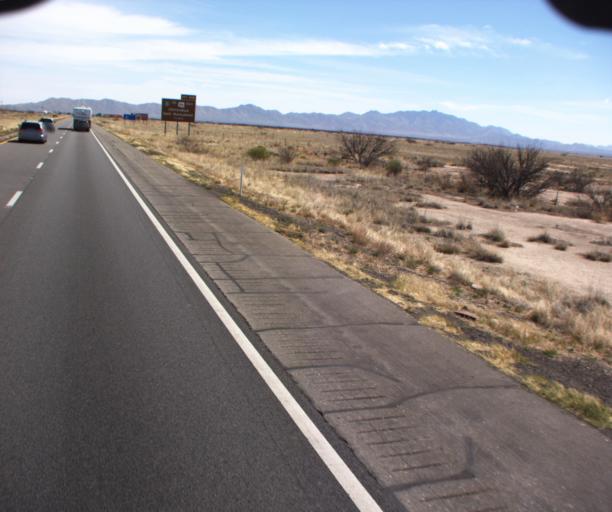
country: US
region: Arizona
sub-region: Cochise County
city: Willcox
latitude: 32.2103
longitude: -109.8922
